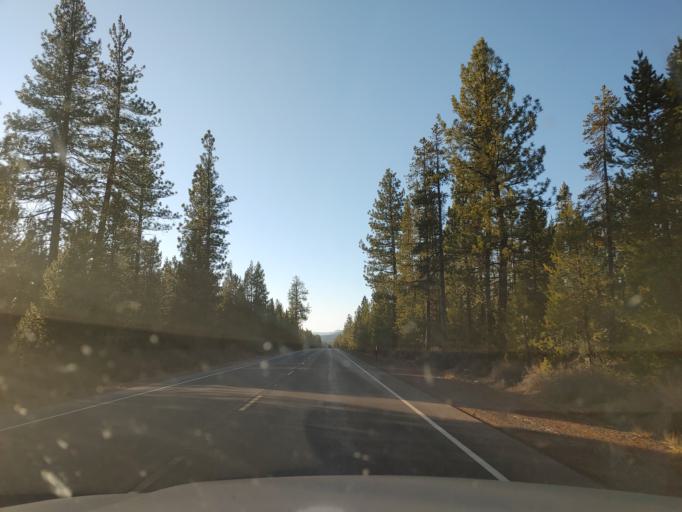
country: US
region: Oregon
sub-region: Deschutes County
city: La Pine
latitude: 43.3920
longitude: -121.8126
